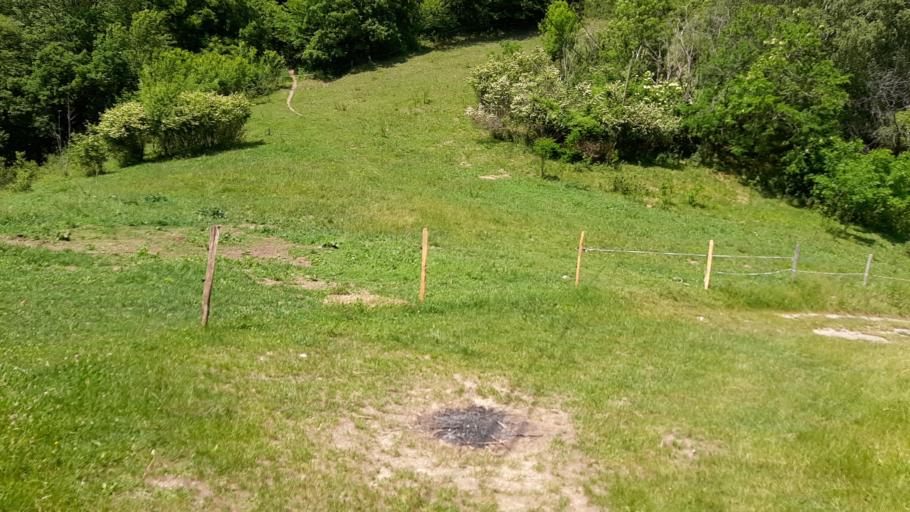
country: FR
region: Rhone-Alpes
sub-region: Departement de la Savoie
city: La Chambre
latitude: 45.3705
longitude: 6.3043
